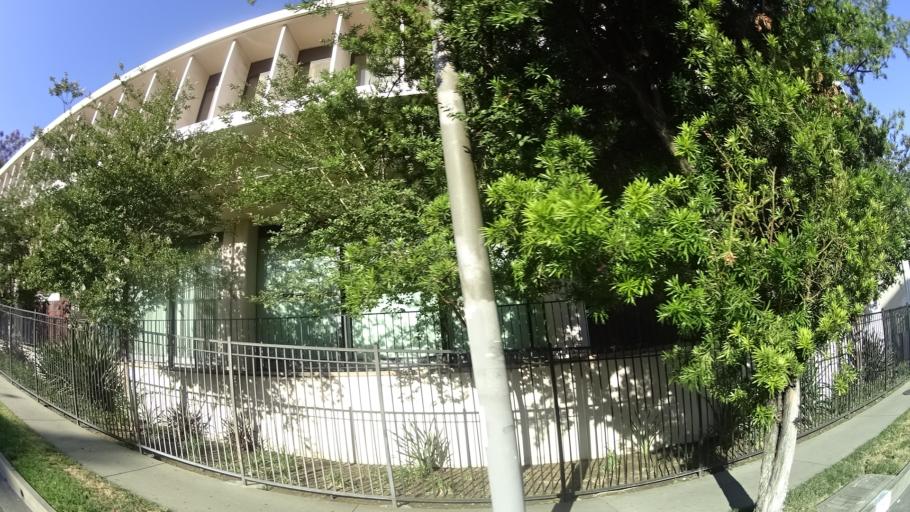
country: US
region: California
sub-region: Los Angeles County
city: Hollywood
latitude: 34.1033
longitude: -118.3457
